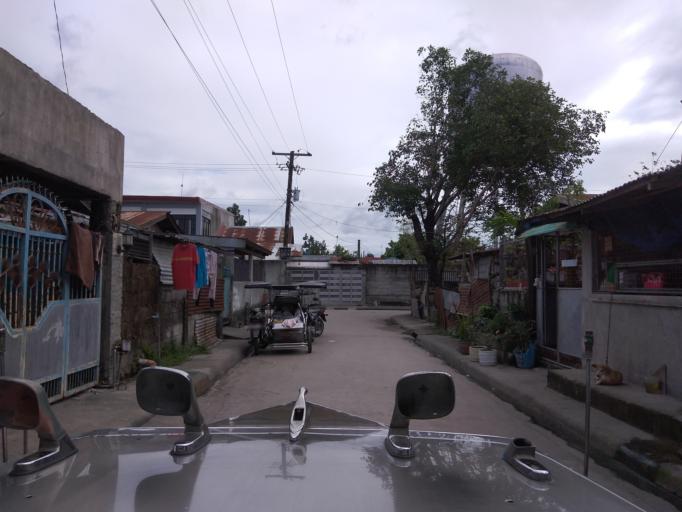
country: PH
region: Central Luzon
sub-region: Province of Pampanga
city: Pandacaqui
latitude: 15.1774
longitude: 120.6568
